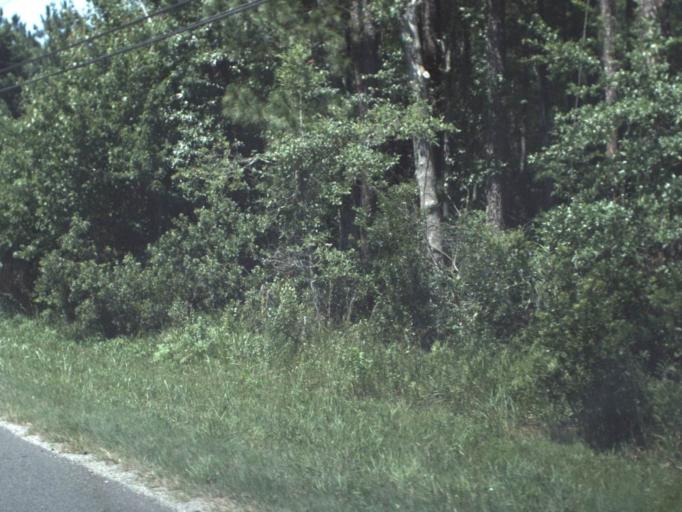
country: US
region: Florida
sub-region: Nassau County
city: Yulee
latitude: 30.6171
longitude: -81.5980
